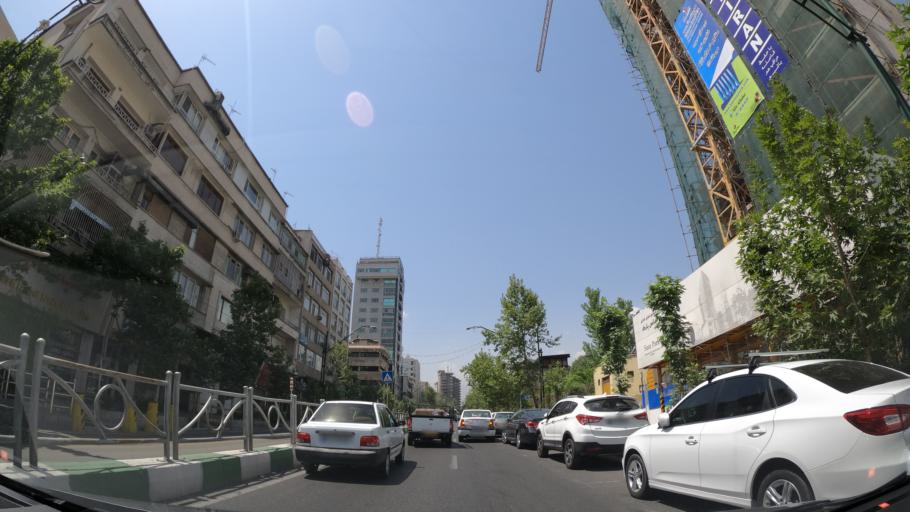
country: IR
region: Tehran
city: Tehran
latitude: 35.7333
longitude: 51.4107
